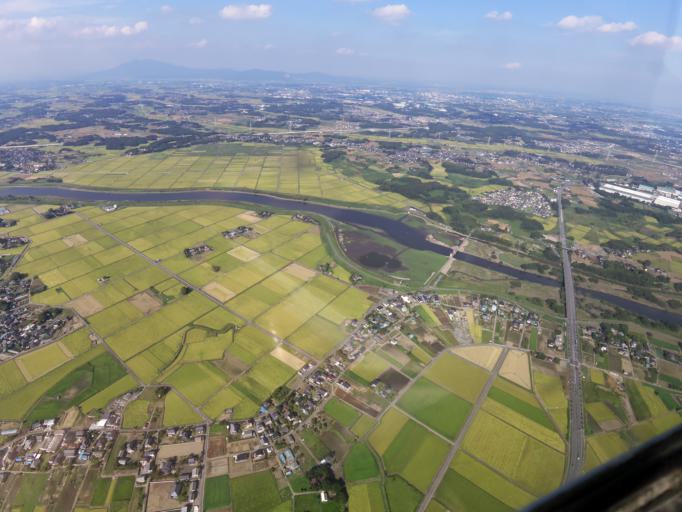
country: JP
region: Ibaraki
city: Mitsukaido
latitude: 36.0396
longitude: 140.0155
